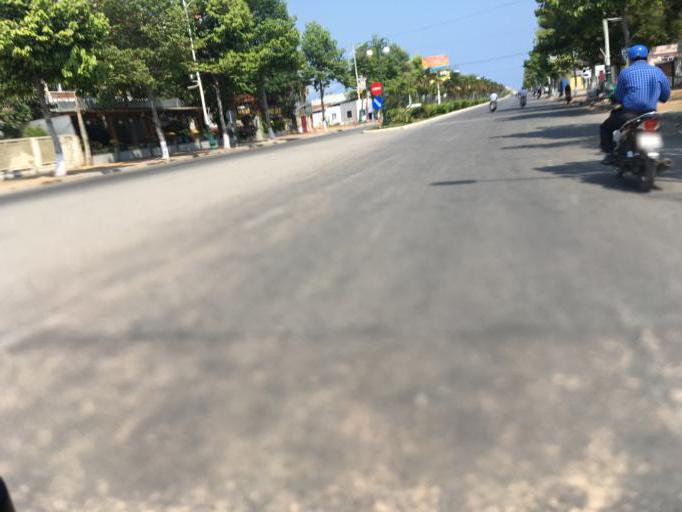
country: VN
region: Ninh Thuan
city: Phan Rang-Thap Cham
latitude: 11.5650
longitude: 109.0011
